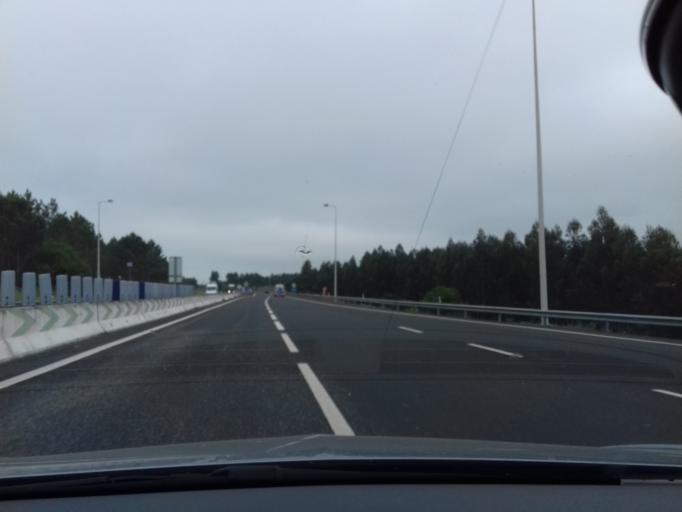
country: PT
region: Leiria
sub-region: Bombarral
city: Bombarral
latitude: 39.2220
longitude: -9.1866
